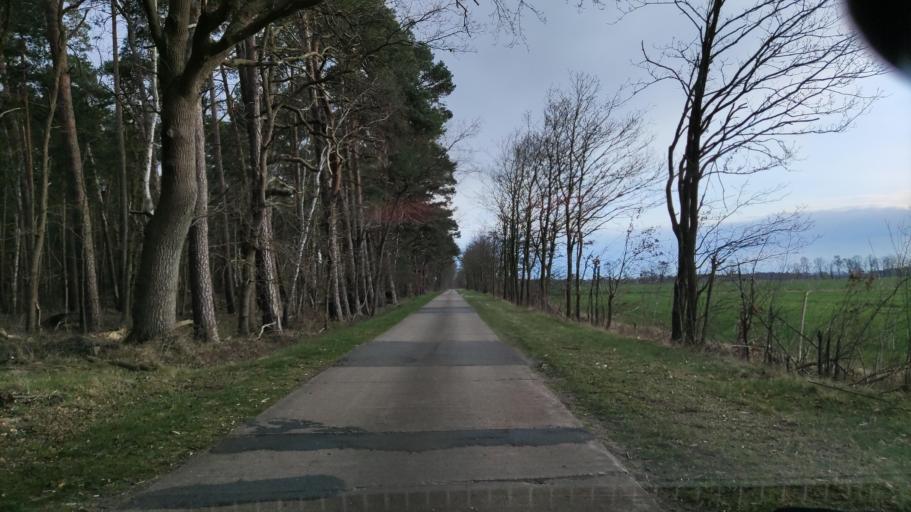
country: DE
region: Lower Saxony
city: Trebel
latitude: 53.0177
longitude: 11.2699
